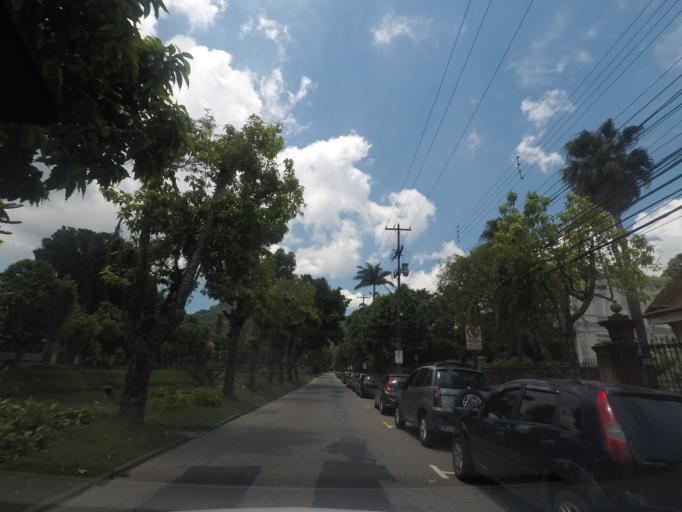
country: BR
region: Rio de Janeiro
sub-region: Petropolis
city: Petropolis
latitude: -22.5083
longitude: -43.1815
